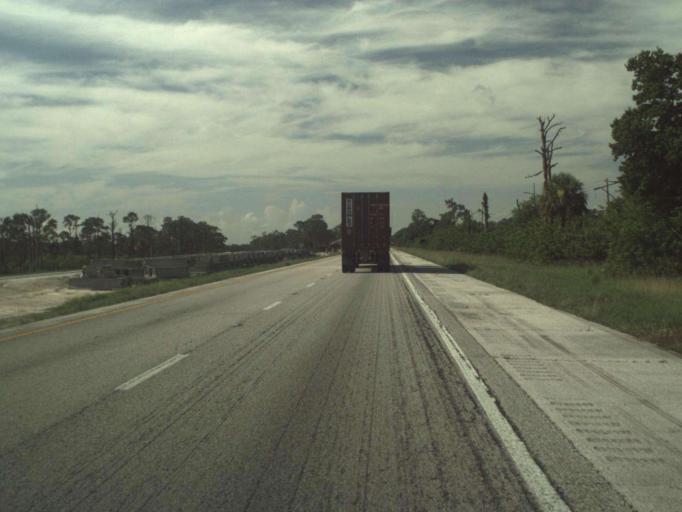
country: US
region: Florida
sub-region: Indian River County
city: West Vero Corridor
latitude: 27.6725
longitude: -80.5314
